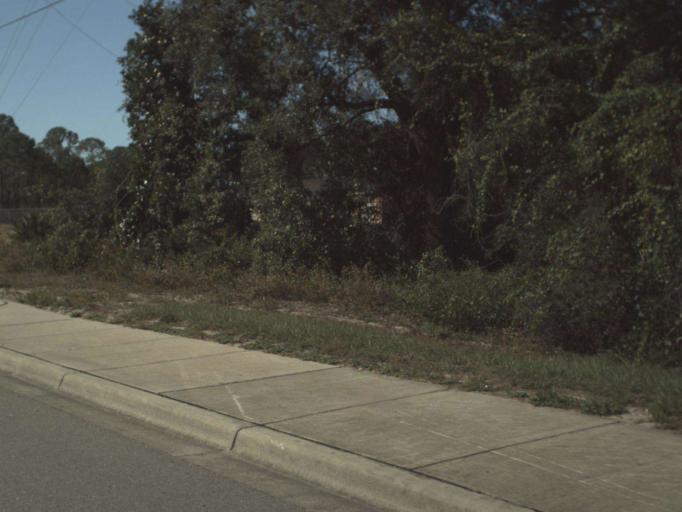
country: US
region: Florida
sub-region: Walton County
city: Seaside
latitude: 30.3773
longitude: -86.1793
